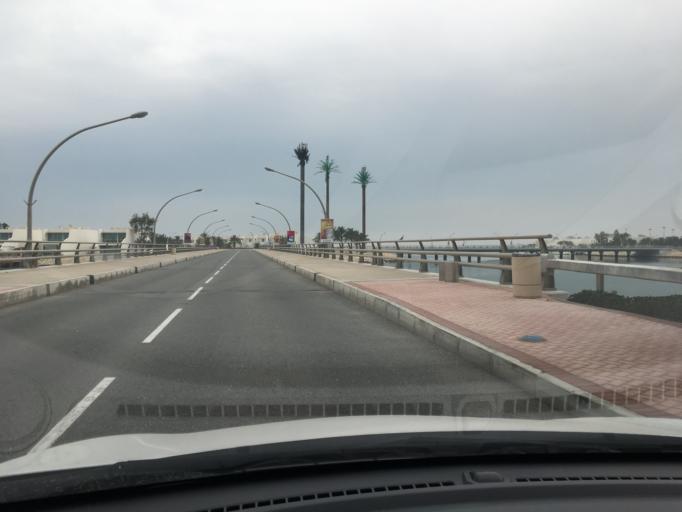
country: BH
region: Central Governorate
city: Dar Kulayb
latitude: 25.8452
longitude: 50.6174
